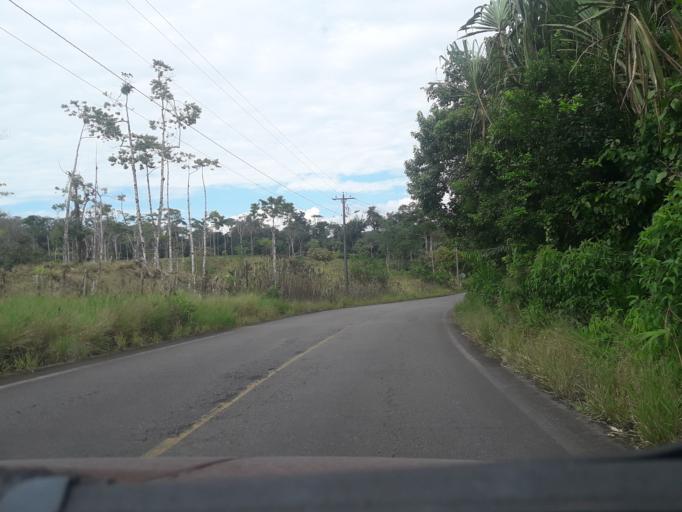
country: EC
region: Napo
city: Tena
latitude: -1.0370
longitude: -77.8918
